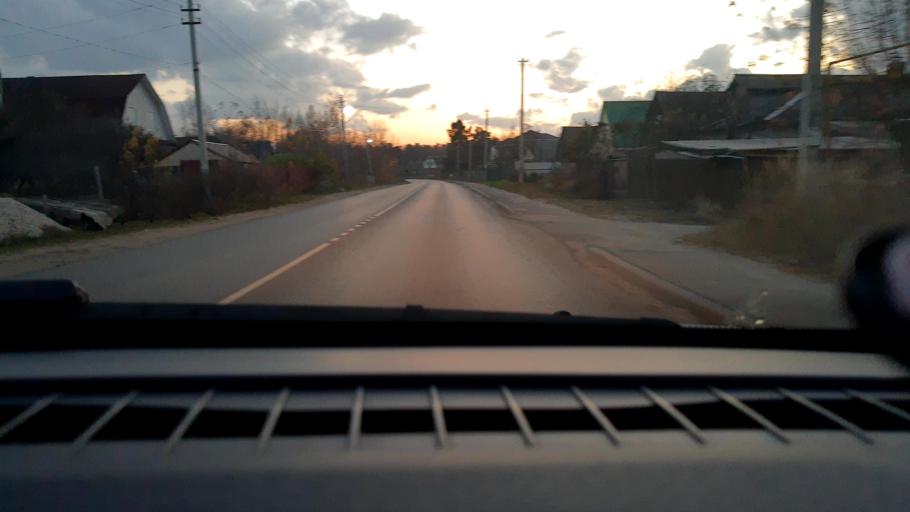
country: RU
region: Nizjnij Novgorod
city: Novaya Balakhna
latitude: 56.4841
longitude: 43.5732
